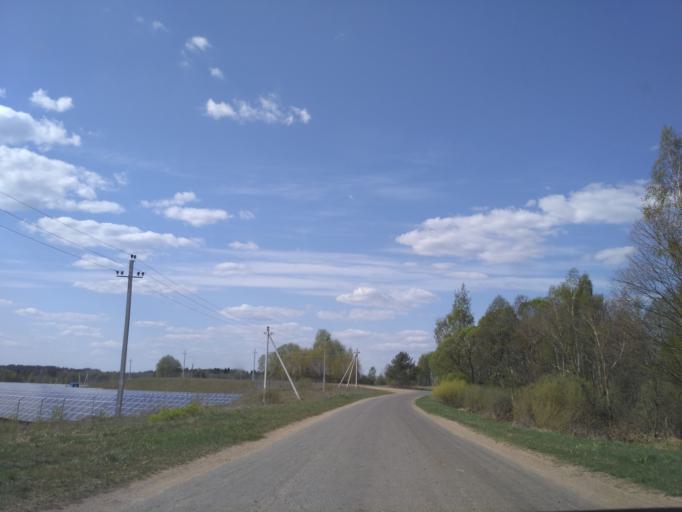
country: BY
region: Minsk
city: Narach
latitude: 54.9652
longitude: 26.6403
